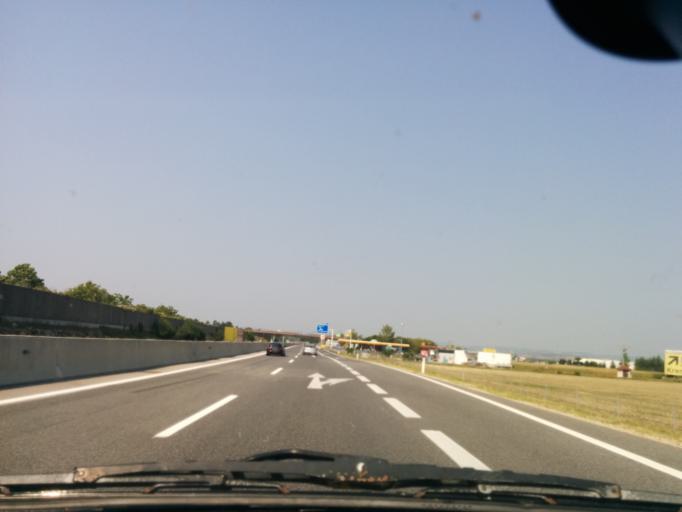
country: AT
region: Lower Austria
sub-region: Politischer Bezirk Tulln
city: Grafenworth
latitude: 48.4114
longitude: 15.7809
